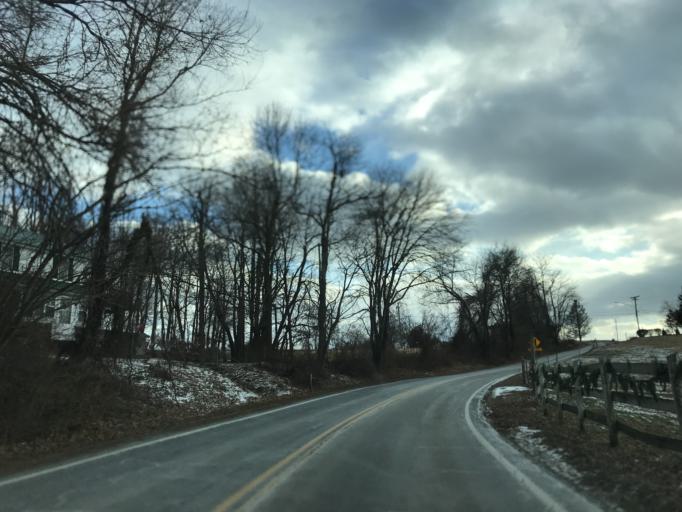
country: US
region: Maryland
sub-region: Harford County
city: Bel Air North
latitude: 39.6179
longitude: -76.3752
